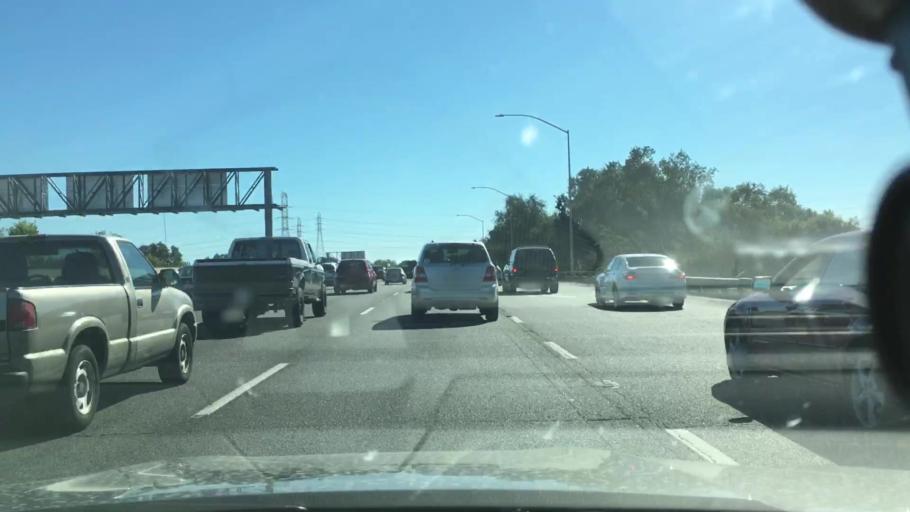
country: US
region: California
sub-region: Sacramento County
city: Sacramento
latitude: 38.5946
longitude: -121.4445
